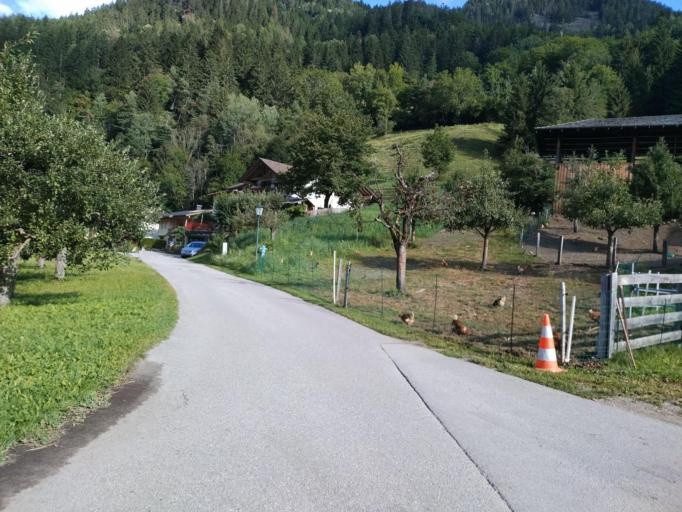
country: AT
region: Tyrol
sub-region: Politischer Bezirk Lienz
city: Hopfgarten in Defereggen
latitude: 46.9301
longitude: 12.5909
